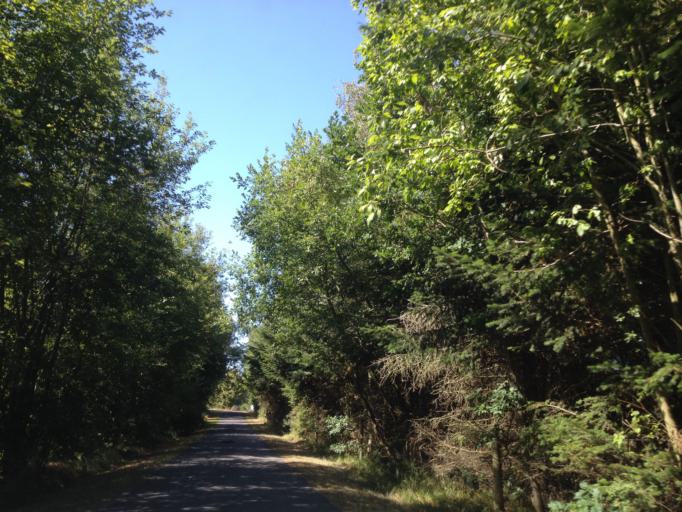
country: DK
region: Capital Region
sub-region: Fredensborg Kommune
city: Humlebaek
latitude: 56.0130
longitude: 12.4794
